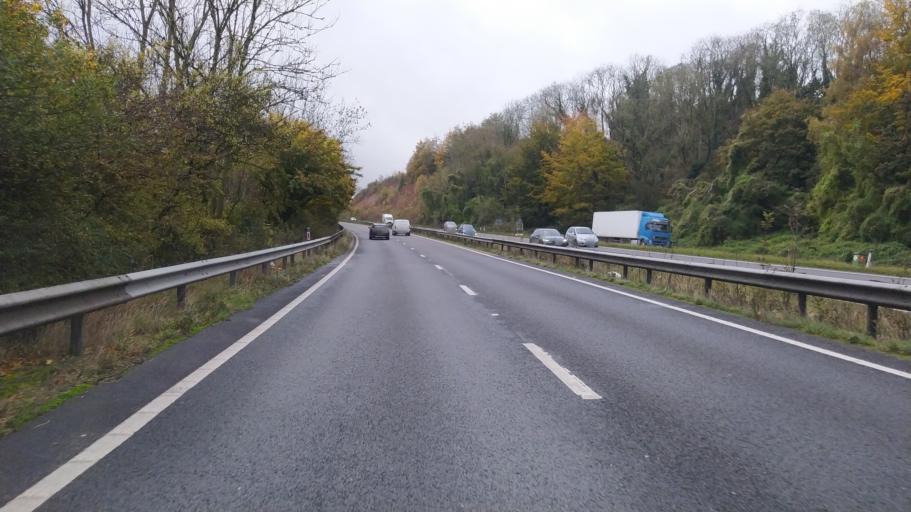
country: GB
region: England
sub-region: Hampshire
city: Petersfield
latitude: 50.9544
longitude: -0.9816
